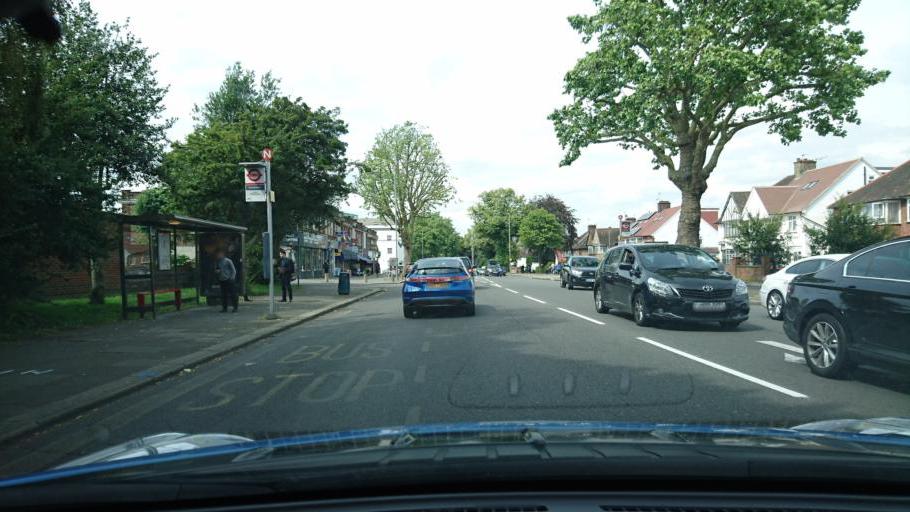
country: GB
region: England
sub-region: Greater London
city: Hendon
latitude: 51.6077
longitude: -0.1751
